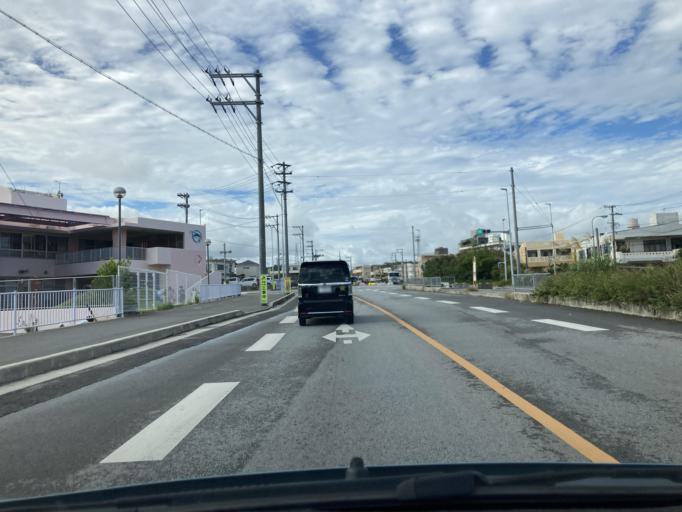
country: JP
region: Okinawa
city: Tomigusuku
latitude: 26.1511
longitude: 127.7228
